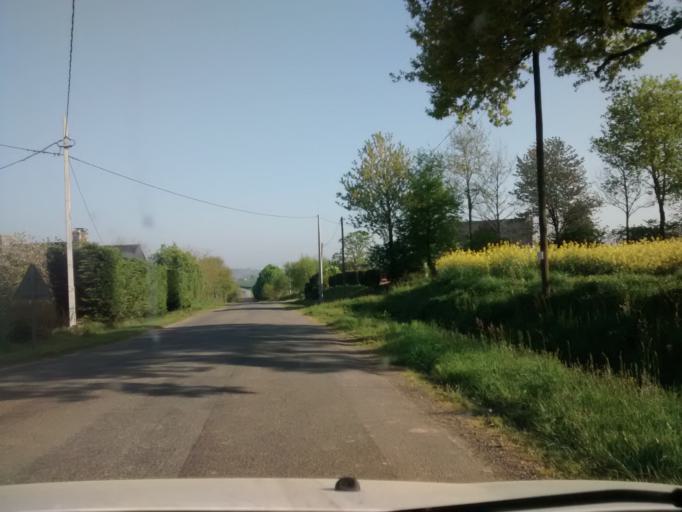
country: FR
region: Brittany
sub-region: Departement d'Ille-et-Vilaine
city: Romagne
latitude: 48.2873
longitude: -1.2985
